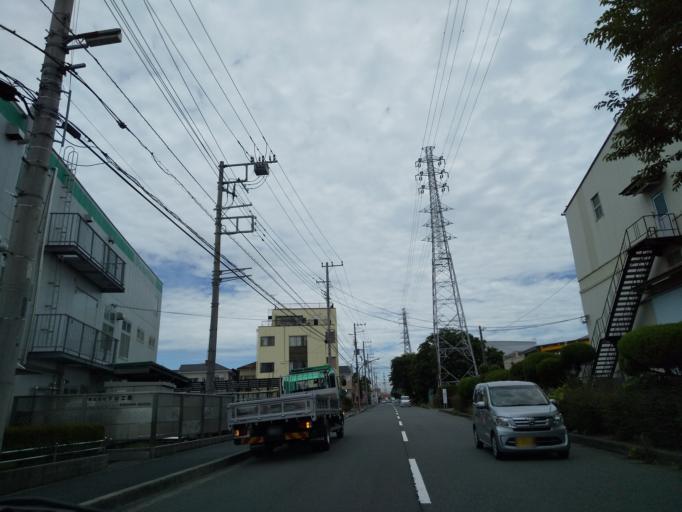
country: JP
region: Kanagawa
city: Zama
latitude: 35.5134
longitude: 139.3411
